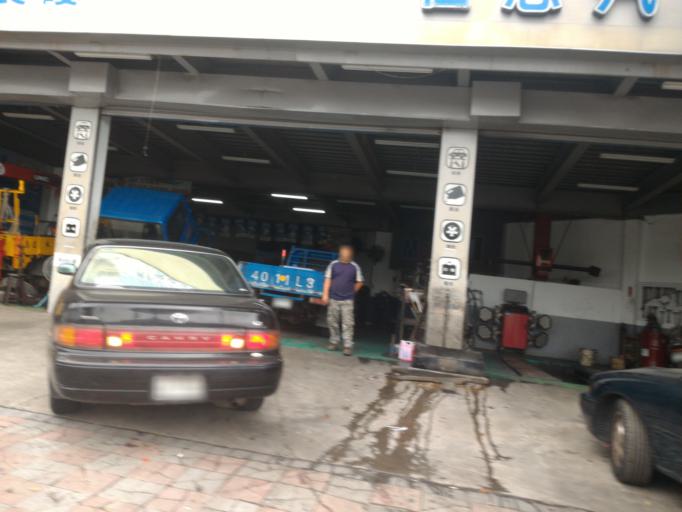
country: TW
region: Taiwan
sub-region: Taoyuan
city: Taoyuan
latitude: 24.9592
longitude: 121.3906
